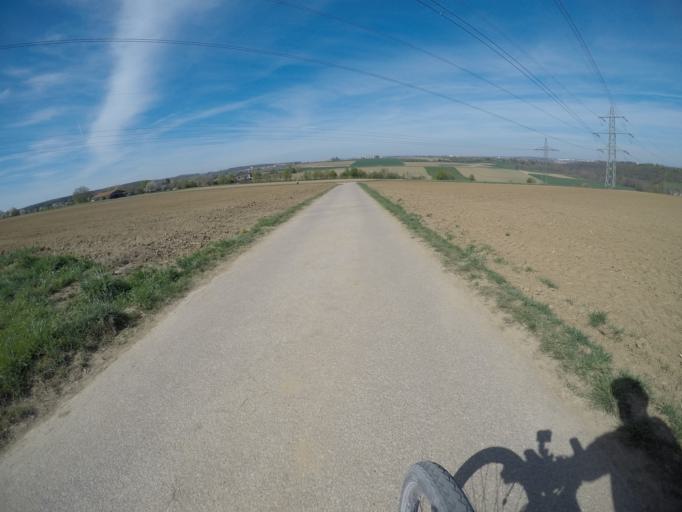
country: DE
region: Baden-Wuerttemberg
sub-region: Regierungsbezirk Stuttgart
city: Hemmingen
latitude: 48.8441
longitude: 9.0407
